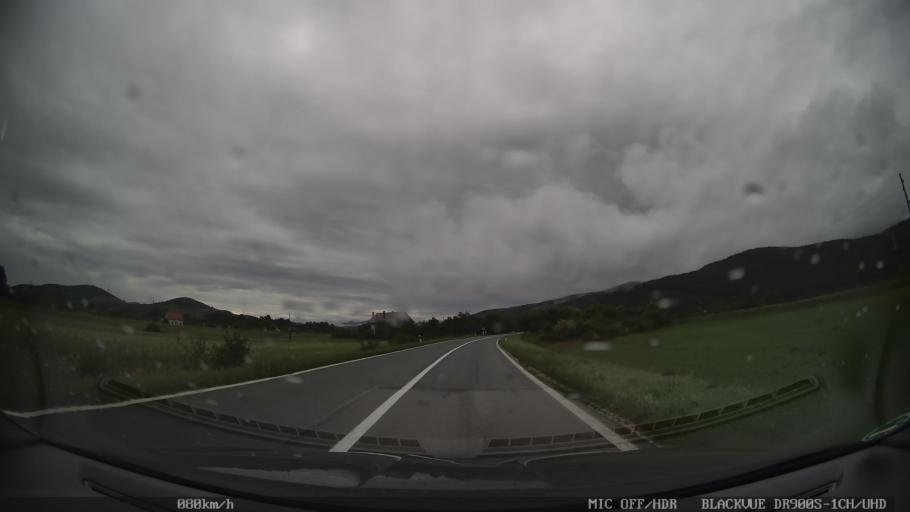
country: HR
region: Licko-Senjska
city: Brinje
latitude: 44.9473
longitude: 15.1260
